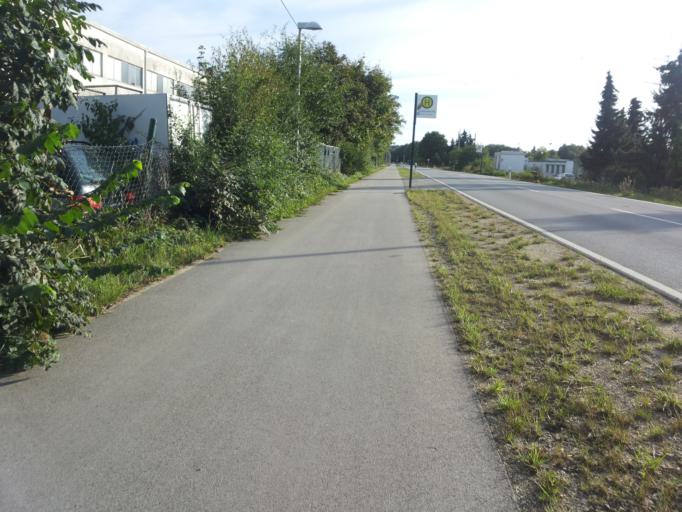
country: DE
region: Bavaria
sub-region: Upper Bavaria
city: Gaimersheim
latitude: 48.7800
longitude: 11.3624
